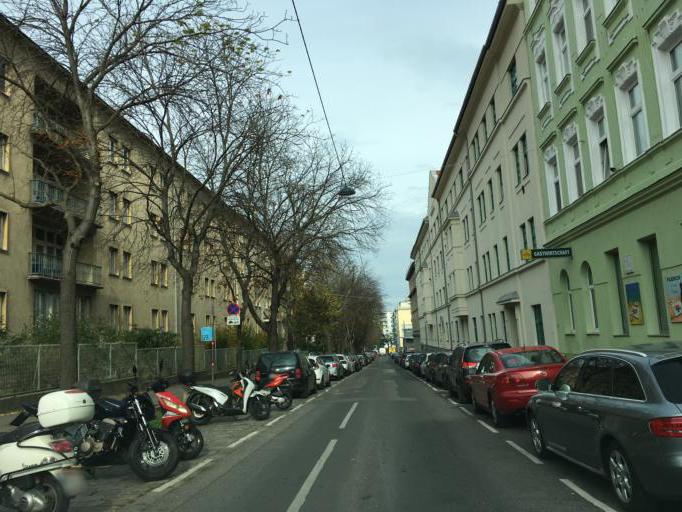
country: AT
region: Vienna
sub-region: Wien Stadt
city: Vienna
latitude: 48.2112
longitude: 16.3045
